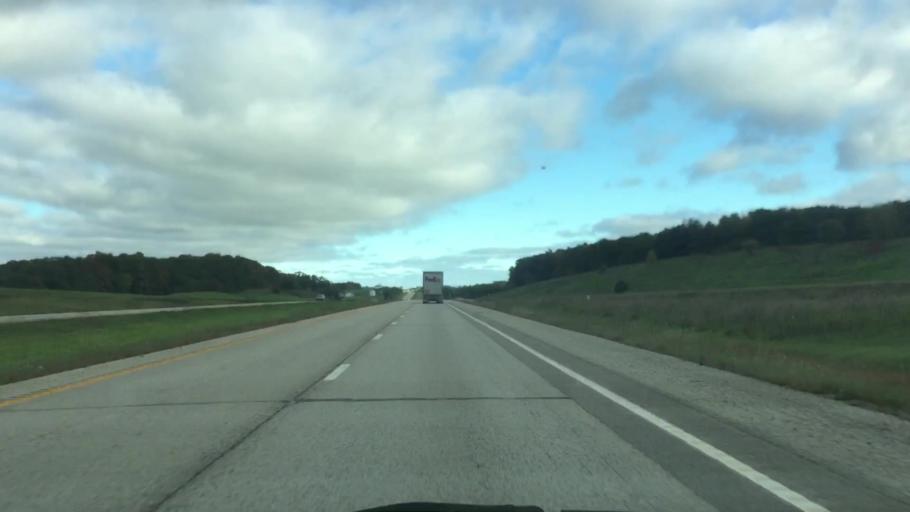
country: US
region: Missouri
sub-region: Harrison County
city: Bethany
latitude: 40.2103
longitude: -94.0134
